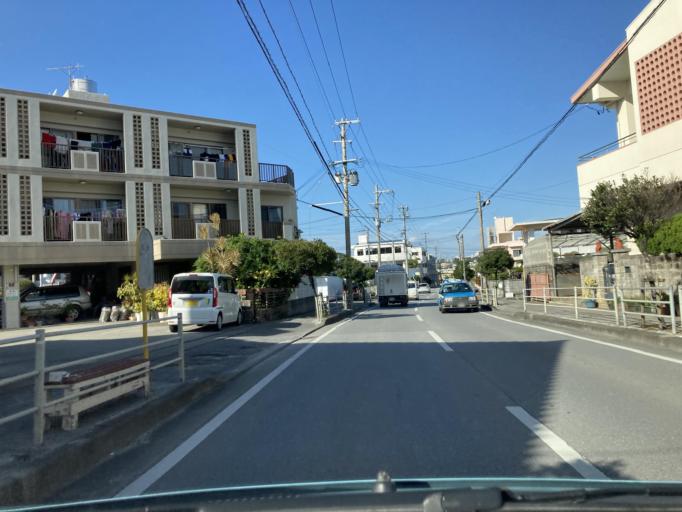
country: JP
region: Okinawa
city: Tomigusuku
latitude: 26.1807
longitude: 127.7068
